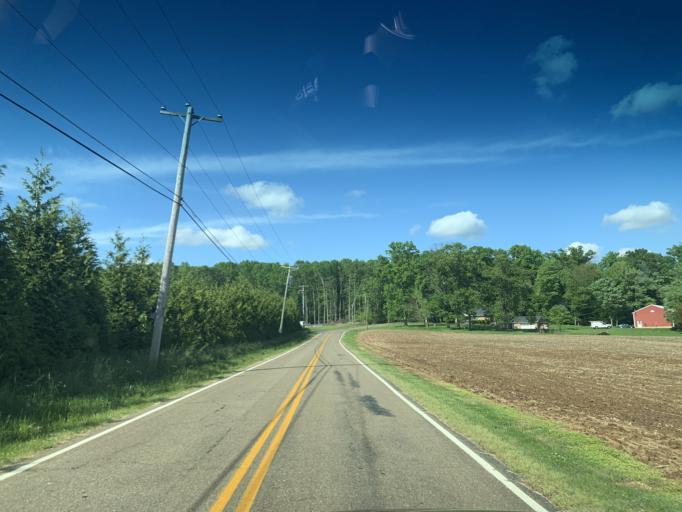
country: US
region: Maryland
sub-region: Cecil County
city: Rising Sun
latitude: 39.7006
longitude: -76.1784
